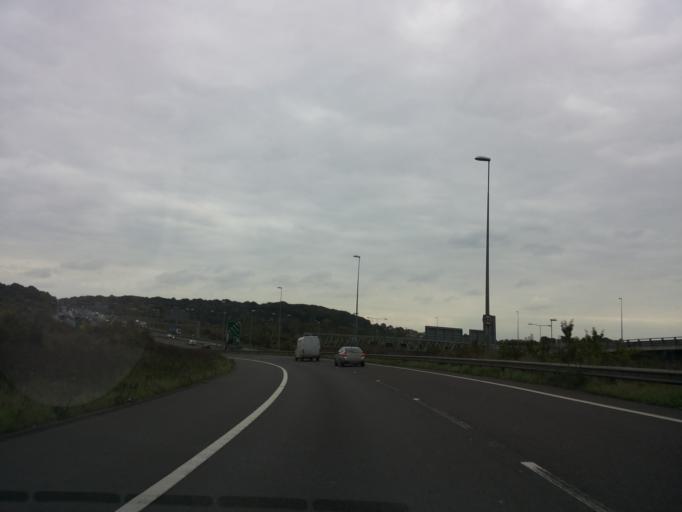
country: GB
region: England
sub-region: Kent
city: Dartford
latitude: 51.4275
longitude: 0.2418
